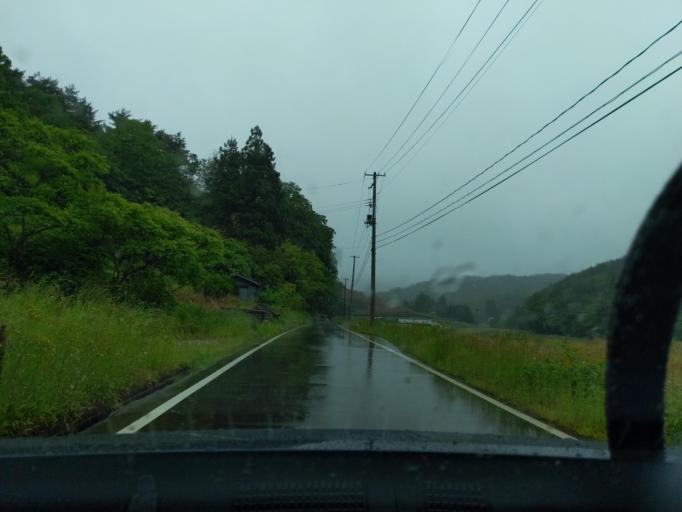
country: JP
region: Fukushima
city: Yanagawamachi-saiwaicho
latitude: 37.6421
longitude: 140.7296
